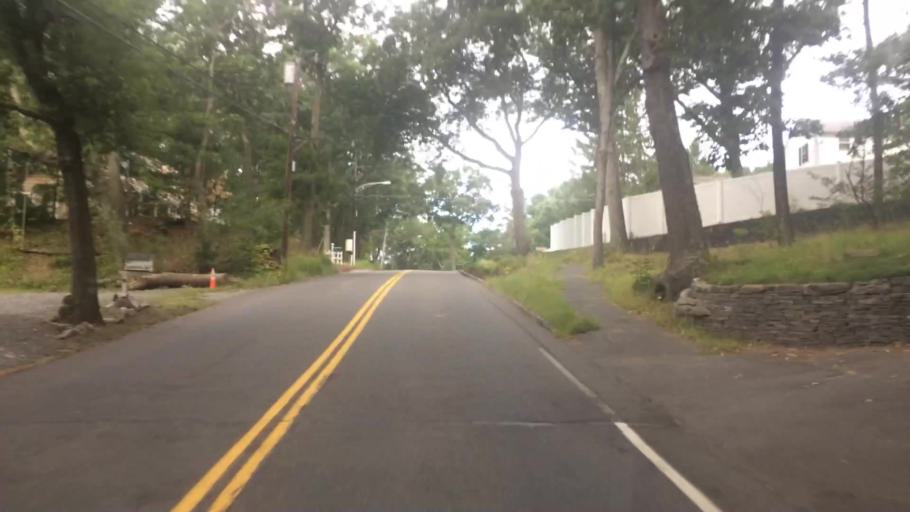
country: US
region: Massachusetts
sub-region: Middlesex County
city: West Concord
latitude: 42.4589
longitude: -71.4087
